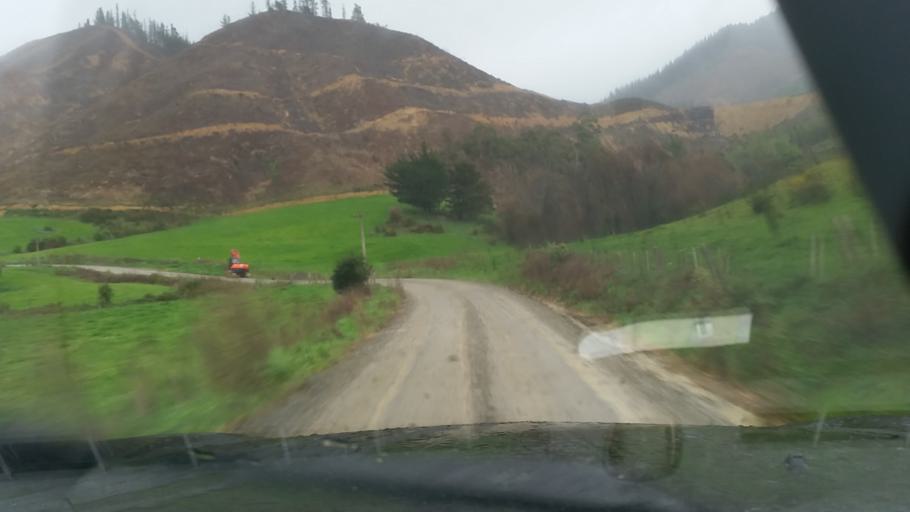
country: NZ
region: Marlborough
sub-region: Marlborough District
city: Picton
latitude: -41.3389
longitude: 173.9271
